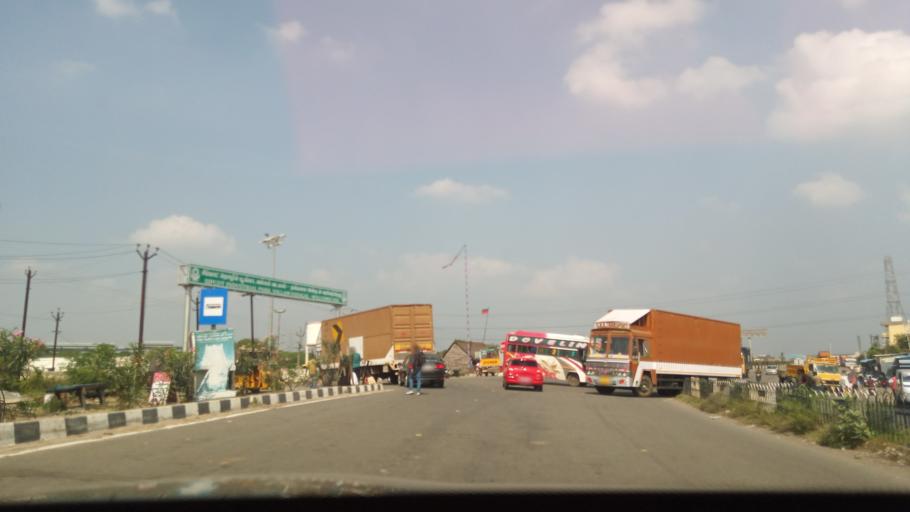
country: IN
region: Tamil Nadu
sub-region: Kancheepuram
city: Sriperumbudur
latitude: 12.8933
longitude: 79.9324
